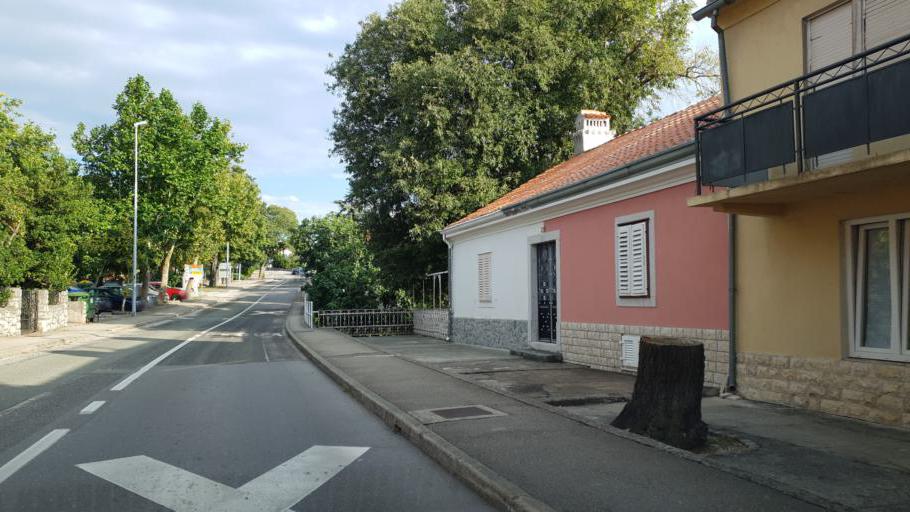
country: HR
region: Primorsko-Goranska
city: Kraljevica
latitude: 45.2730
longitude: 14.5704
